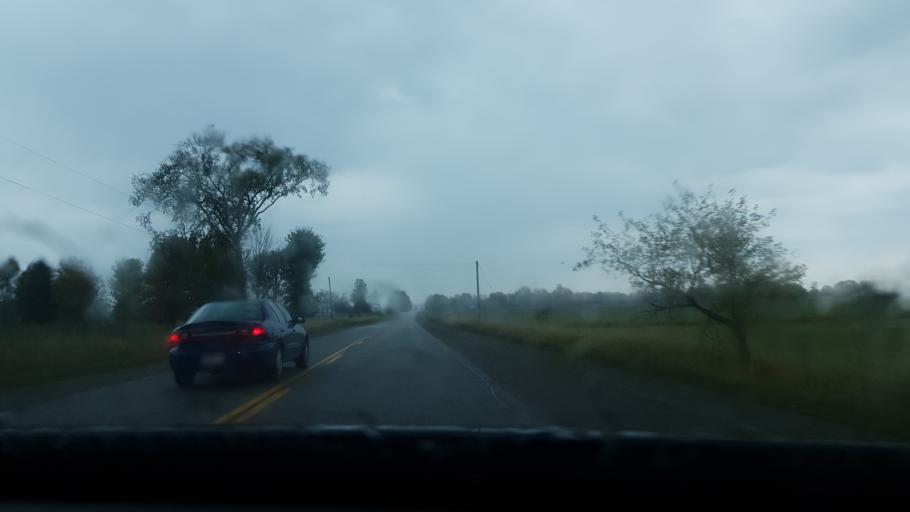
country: CA
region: Ontario
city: Omemee
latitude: 44.3860
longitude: -78.5929
